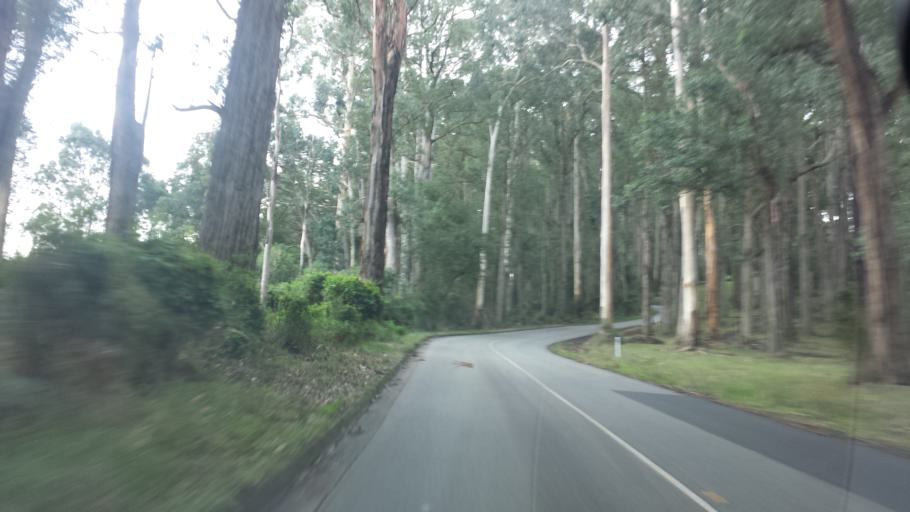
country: AU
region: Victoria
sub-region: Yarra Ranges
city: Belgrave
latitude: -37.8921
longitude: 145.3463
